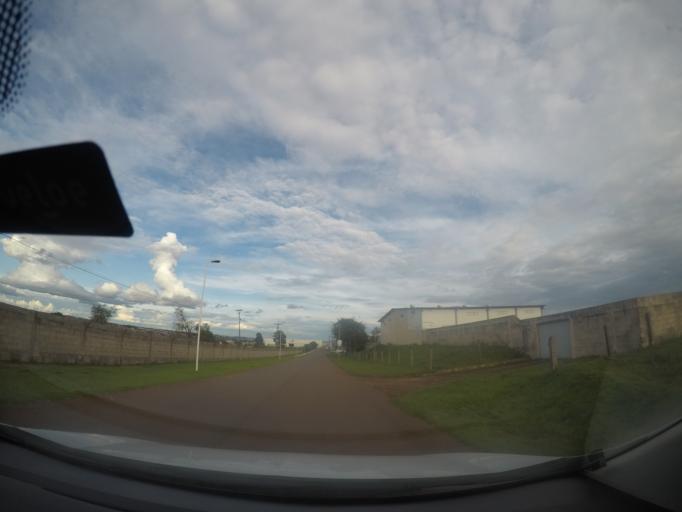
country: BR
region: Goias
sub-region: Goiania
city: Goiania
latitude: -16.6230
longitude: -49.3518
